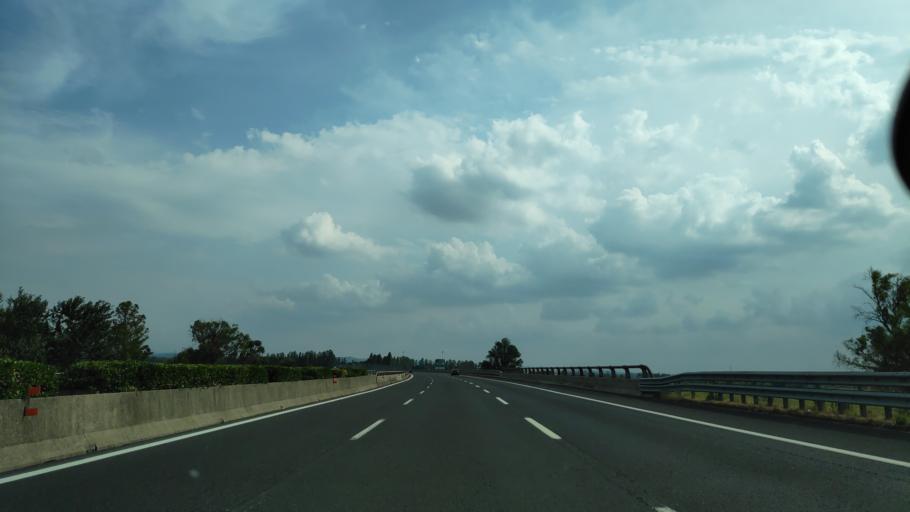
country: IT
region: Latium
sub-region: Citta metropolitana di Roma Capitale
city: Bivio di Capanelle
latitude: 42.1324
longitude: 12.6175
